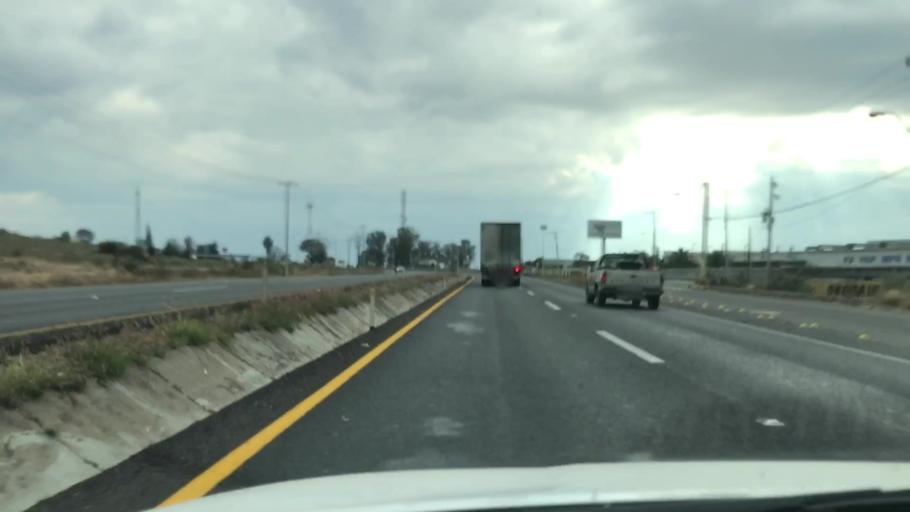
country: MX
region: Guanajuato
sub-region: Irapuato
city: San Ignacio de Rivera (Ojo de Agua)
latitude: 20.5689
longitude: -101.4452
